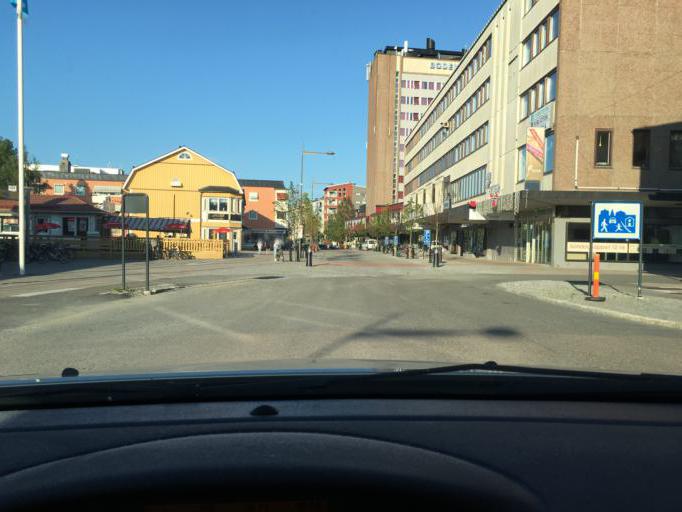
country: SE
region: Norrbotten
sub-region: Bodens Kommun
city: Boden
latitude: 65.8249
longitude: 21.6848
